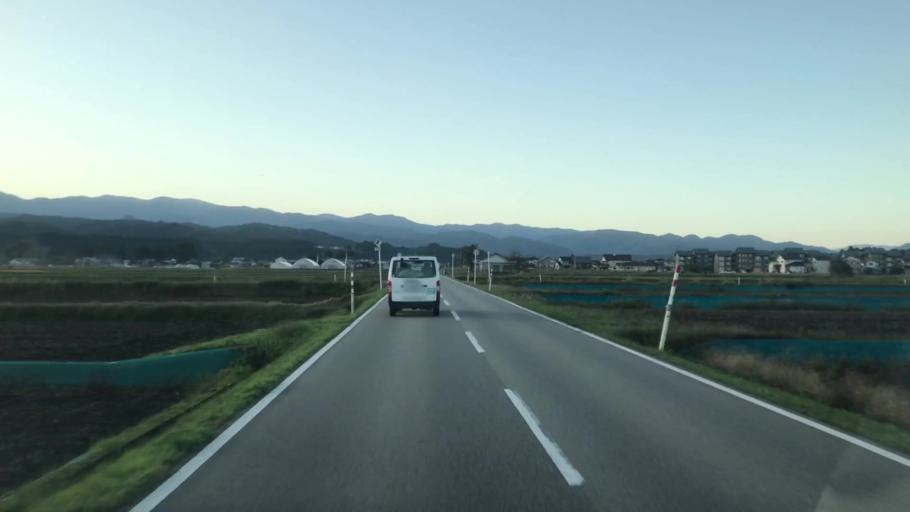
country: JP
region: Toyama
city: Kamiichi
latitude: 36.6367
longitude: 137.3285
